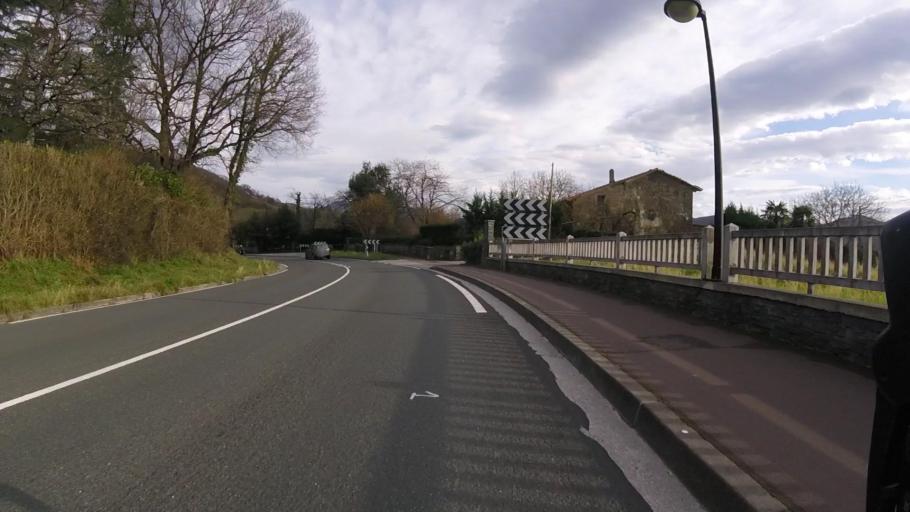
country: ES
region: Basque Country
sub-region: Provincia de Guipuzcoa
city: Lezo
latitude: 43.3023
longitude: -1.8714
